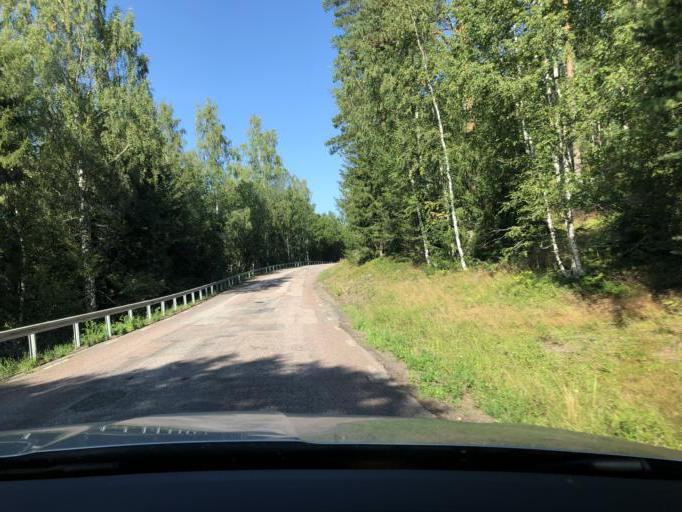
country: SE
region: Dalarna
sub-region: Hedemora Kommun
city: Hedemora
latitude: 60.3396
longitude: 15.9213
